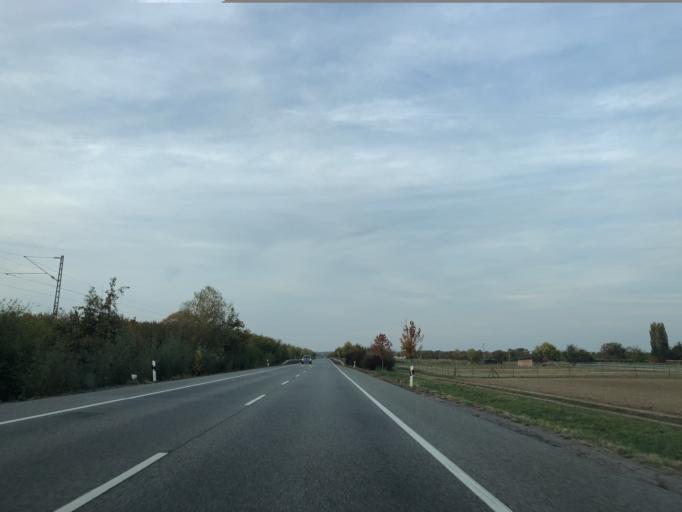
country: DE
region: Rheinland-Pfalz
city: Dienheim
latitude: 49.8306
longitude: 8.3554
